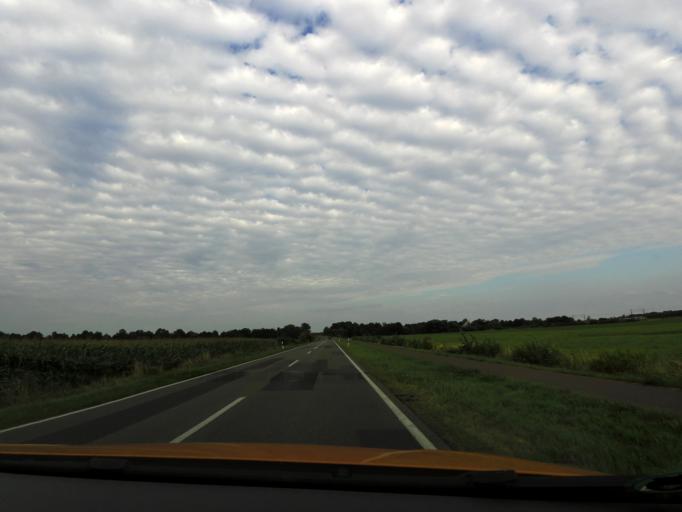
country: DE
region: Brandenburg
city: Brandenburg an der Havel
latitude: 52.4110
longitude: 12.6253
